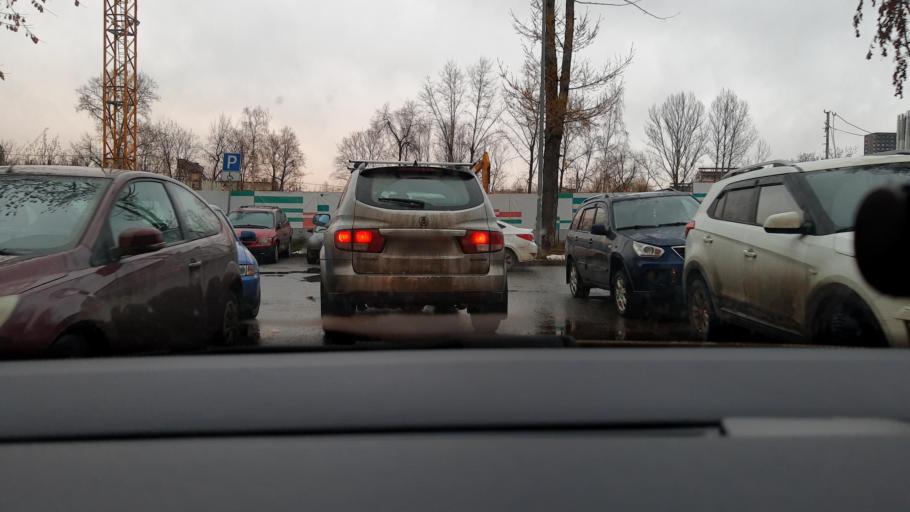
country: RU
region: Moscow
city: Kozeyevo
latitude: 55.8781
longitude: 37.6281
